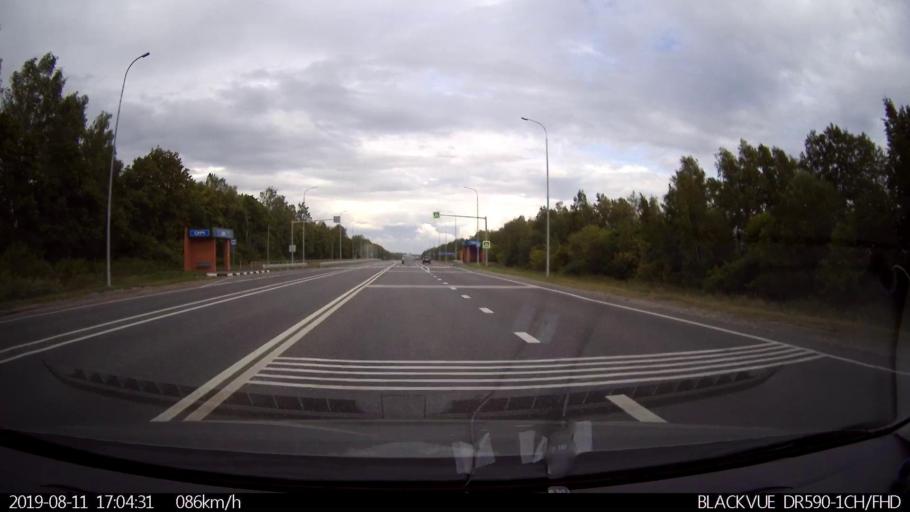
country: RU
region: Ulyanovsk
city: Mayna
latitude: 54.3005
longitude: 47.7656
